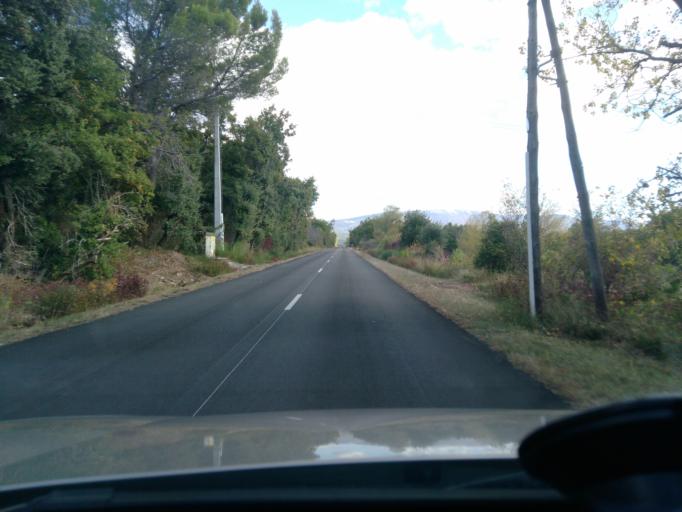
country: FR
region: Rhone-Alpes
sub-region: Departement de la Drome
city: Grignan
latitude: 44.4359
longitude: 4.9301
